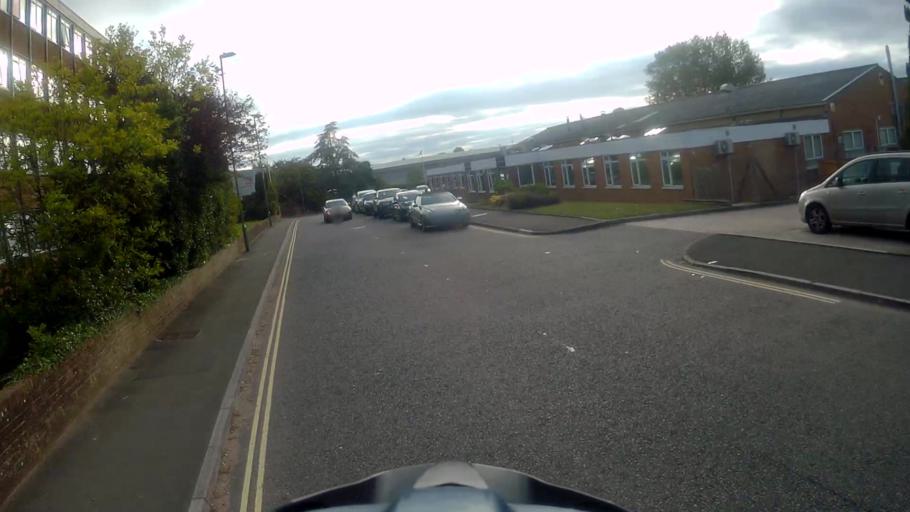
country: GB
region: England
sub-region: Hampshire
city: Basingstoke
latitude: 51.2530
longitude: -1.1030
